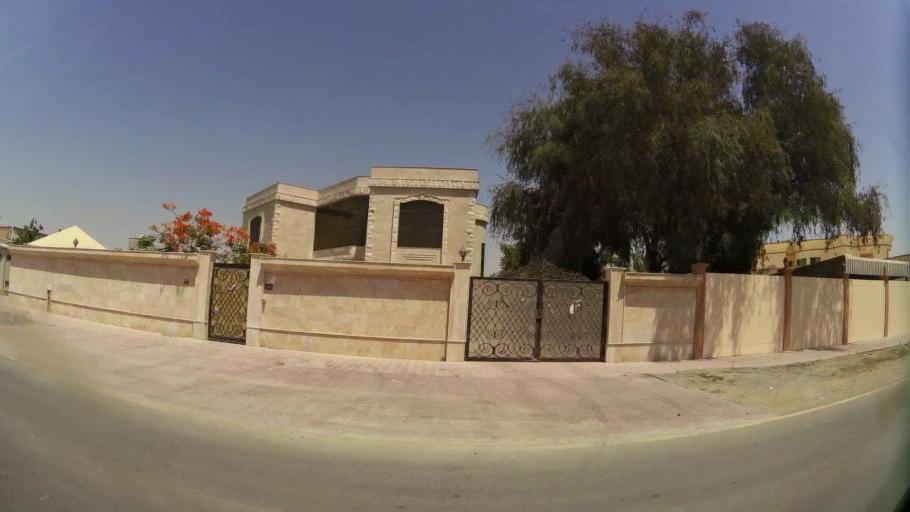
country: AE
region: Ajman
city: Ajman
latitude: 25.4277
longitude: 55.5089
